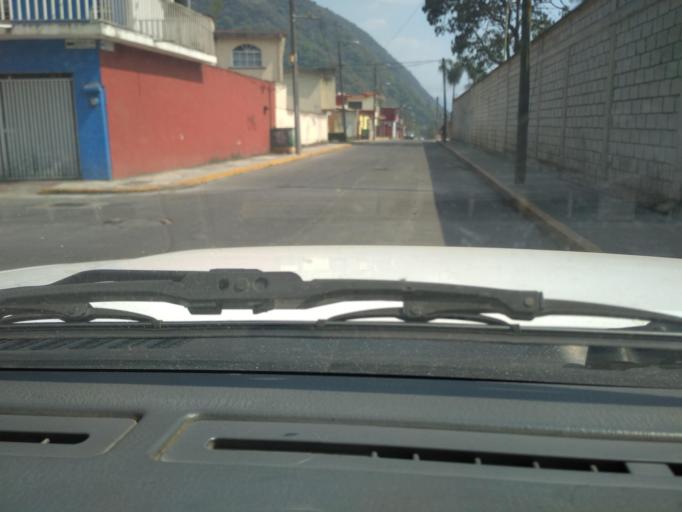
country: MX
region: Veracruz
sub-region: Mariano Escobedo
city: Palmira
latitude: 18.8737
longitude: -97.0978
